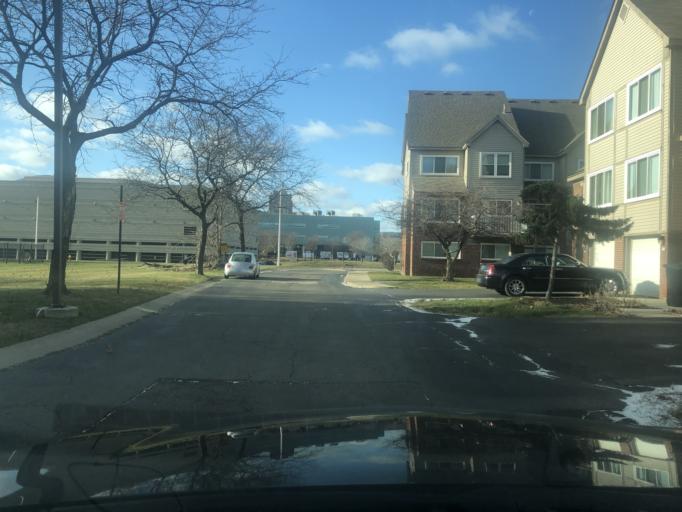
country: US
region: Michigan
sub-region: Wayne County
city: Detroit
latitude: 42.3603
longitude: -83.0598
